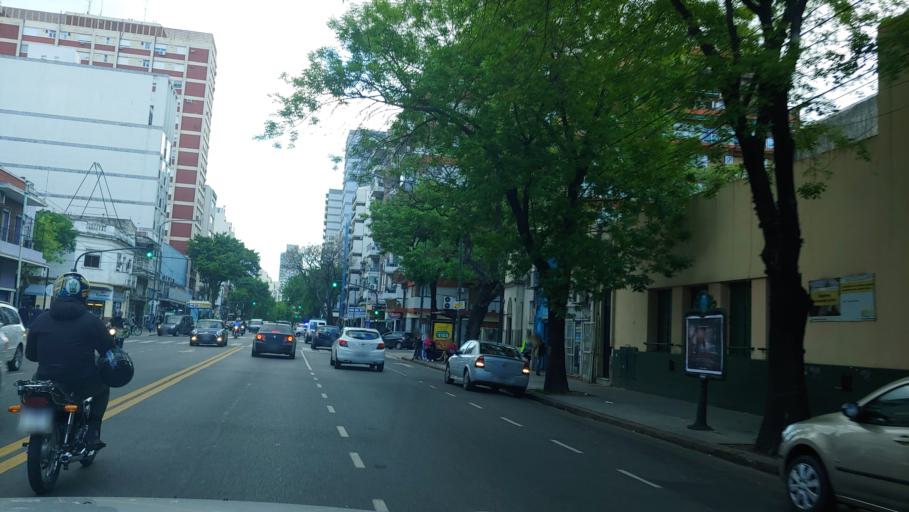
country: AR
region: Buenos Aires F.D.
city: Colegiales
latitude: -34.5755
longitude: -58.4481
